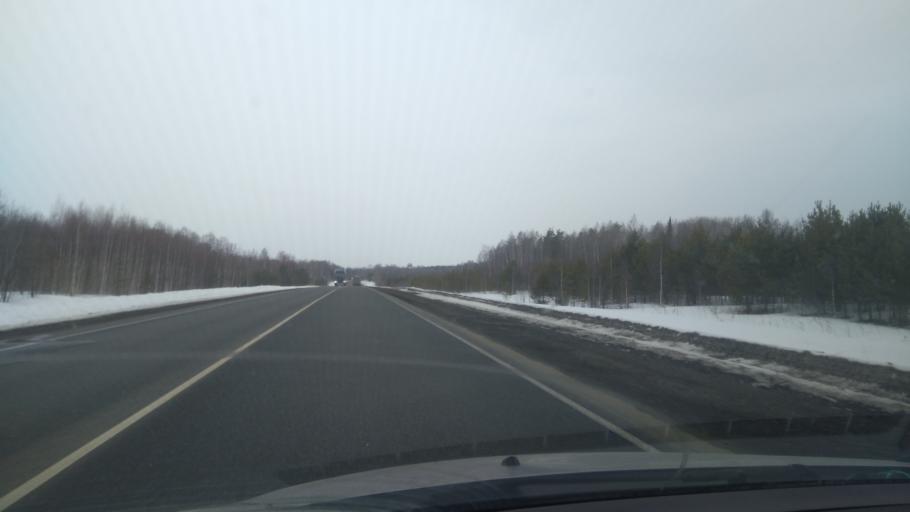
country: RU
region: Perm
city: Suksun
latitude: 56.9899
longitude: 57.4930
